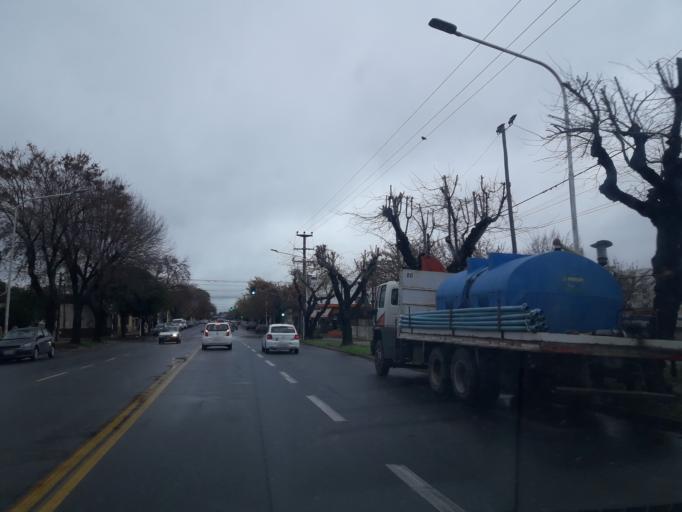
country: AR
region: Buenos Aires
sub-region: Partido de Tandil
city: Tandil
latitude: -37.3252
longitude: -59.1475
